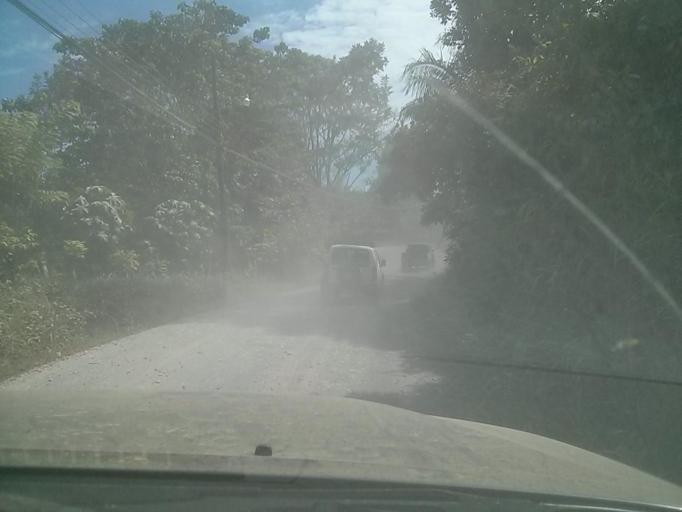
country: CR
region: Puntarenas
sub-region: Canton de Golfito
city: Golfito
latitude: 8.4543
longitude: -83.0537
